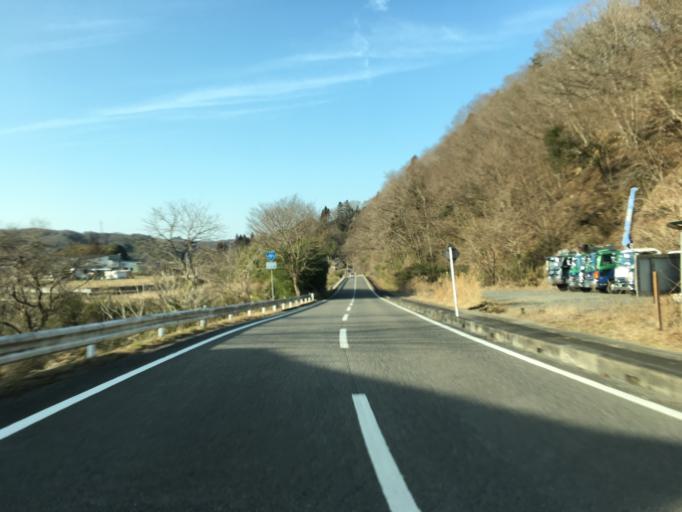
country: JP
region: Ibaraki
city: Daigo
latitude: 36.7633
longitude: 140.4336
